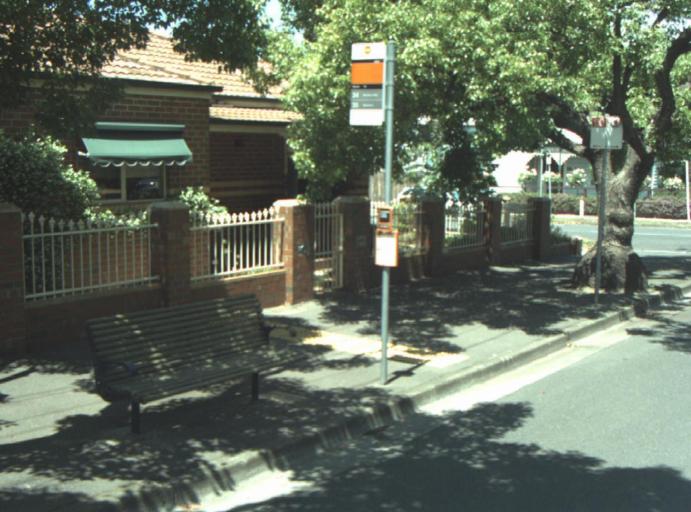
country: AU
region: Victoria
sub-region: Greater Geelong
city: Geelong West
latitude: -38.1543
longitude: 144.3457
